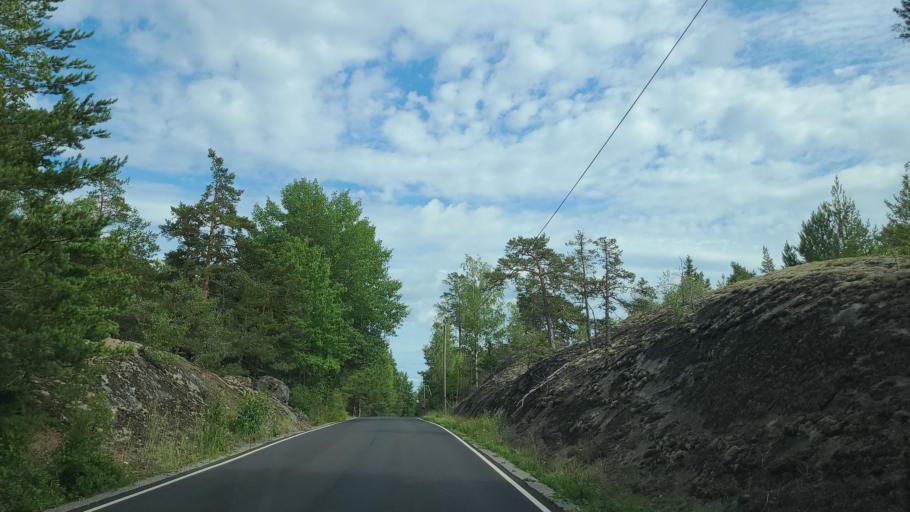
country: FI
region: Varsinais-Suomi
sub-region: Turku
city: Rymaettylae
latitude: 60.3199
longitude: 21.9591
